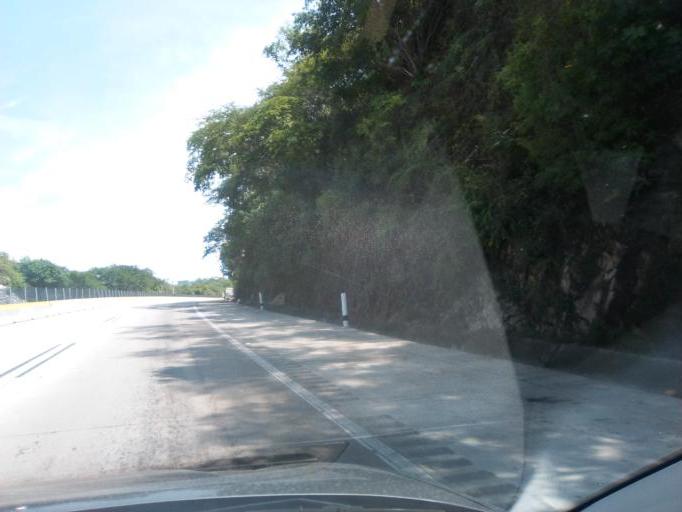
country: MX
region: Guerrero
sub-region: Acapulco de Juarez
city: Colonia Nueva Revolucion
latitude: 16.9290
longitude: -99.7997
